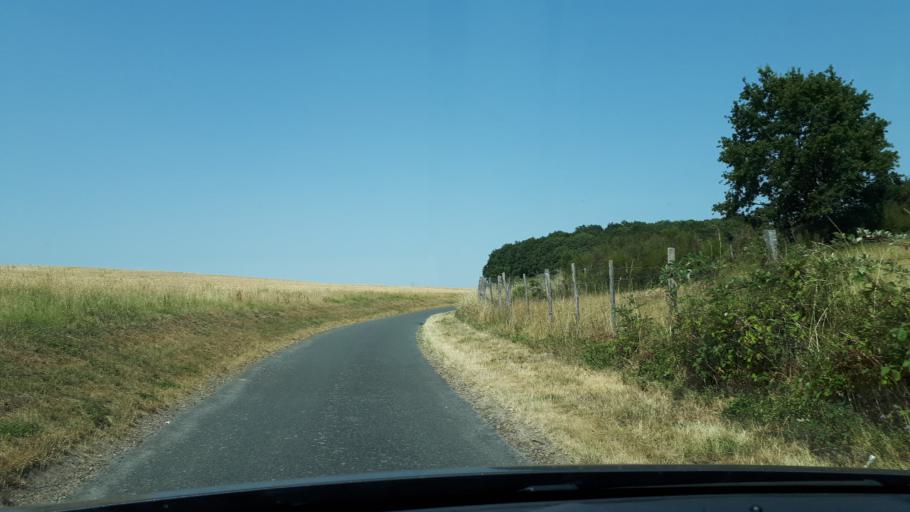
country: FR
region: Centre
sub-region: Departement du Loir-et-Cher
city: Saint-Ouen
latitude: 47.8200
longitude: 1.0641
